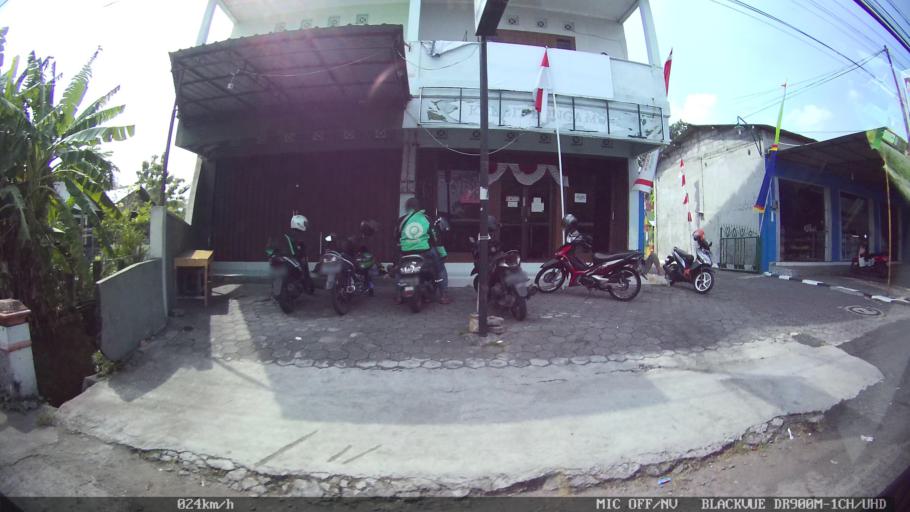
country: ID
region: Daerah Istimewa Yogyakarta
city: Depok
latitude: -7.8043
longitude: 110.4407
